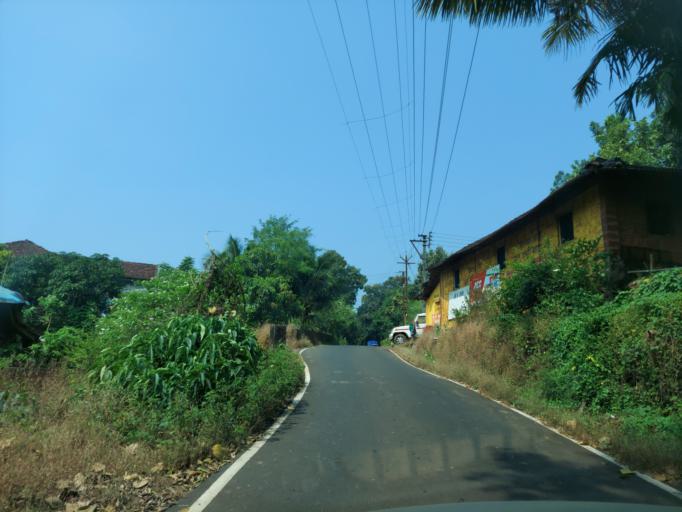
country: IN
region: Maharashtra
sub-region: Sindhudurg
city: Malvan
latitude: 15.9882
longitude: 73.5293
